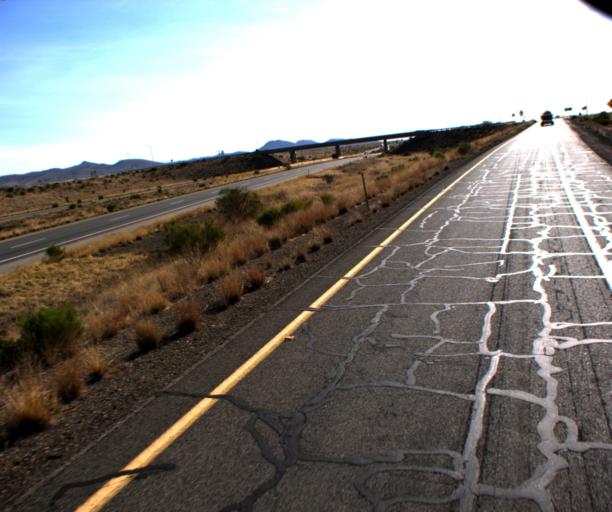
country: US
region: Arizona
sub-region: Cochise County
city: Willcox
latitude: 32.3582
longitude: -109.6841
